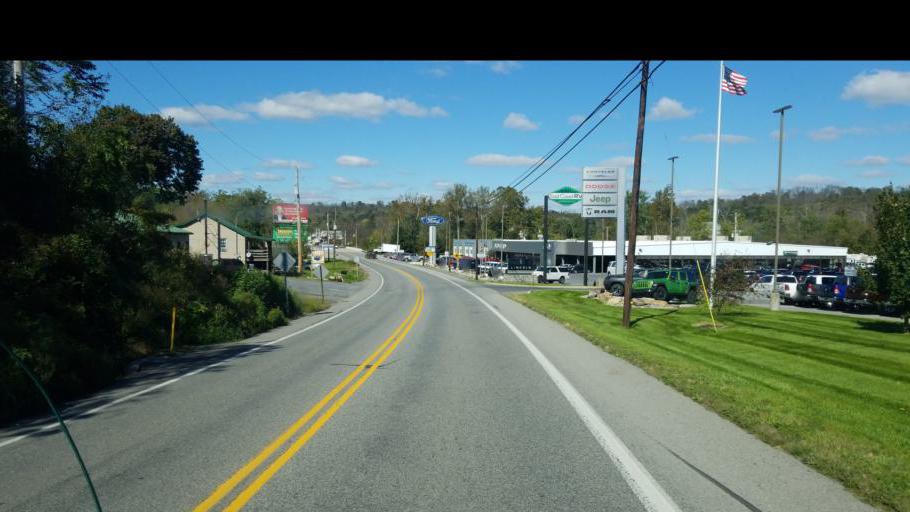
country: US
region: Pennsylvania
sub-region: Bedford County
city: Bedford
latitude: 40.0444
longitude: -78.5272
